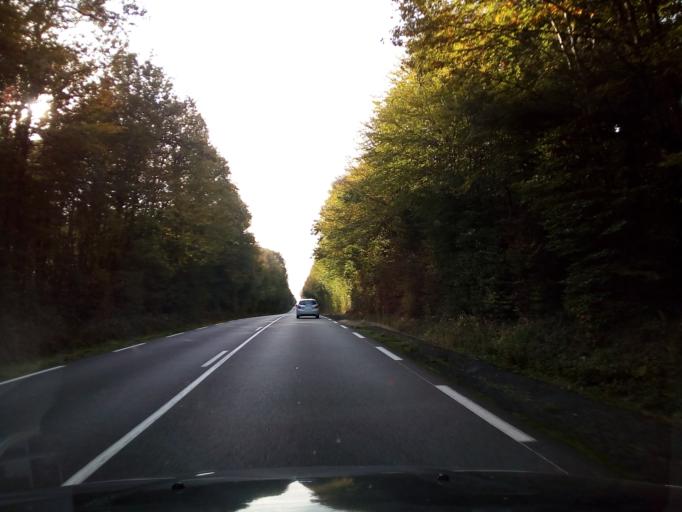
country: FR
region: Limousin
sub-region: Departement de la Haute-Vienne
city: Peyrat-de-Bellac
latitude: 46.1163
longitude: 0.9442
